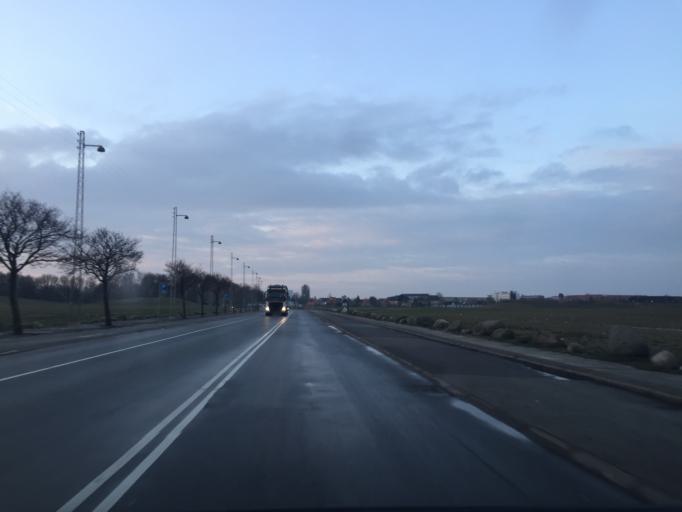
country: DK
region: Capital Region
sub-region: Tarnby Kommune
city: Tarnby
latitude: 55.6451
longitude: 12.6439
